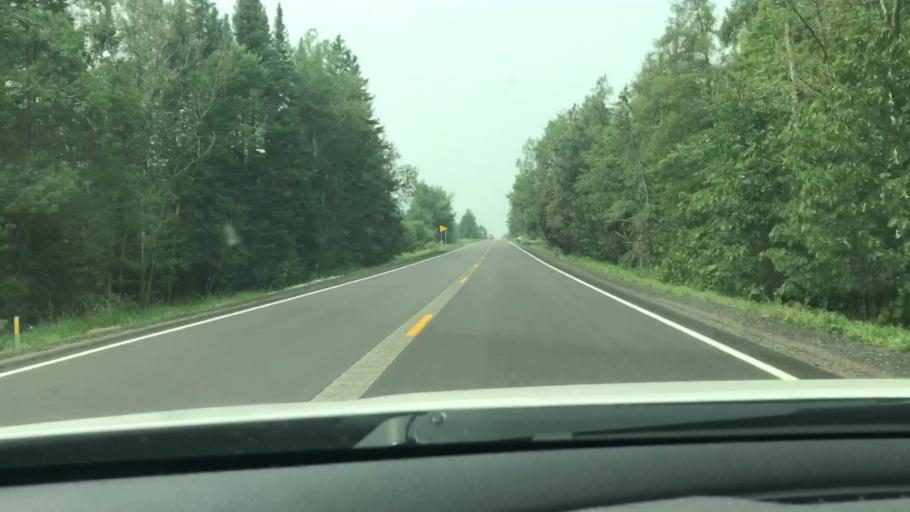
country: US
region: Minnesota
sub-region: Itasca County
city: Cohasset
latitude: 47.3581
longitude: -93.8569
